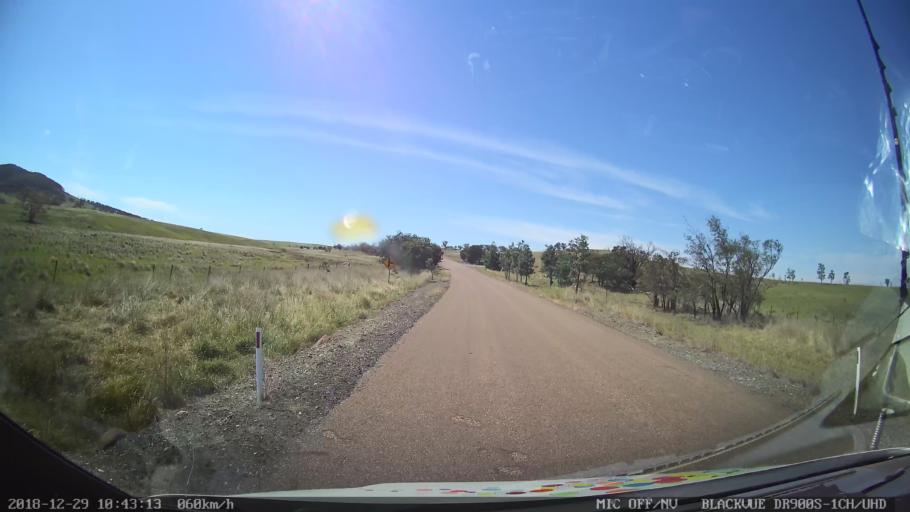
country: AU
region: New South Wales
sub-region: Palerang
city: Bungendore
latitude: -35.0393
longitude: 149.5363
